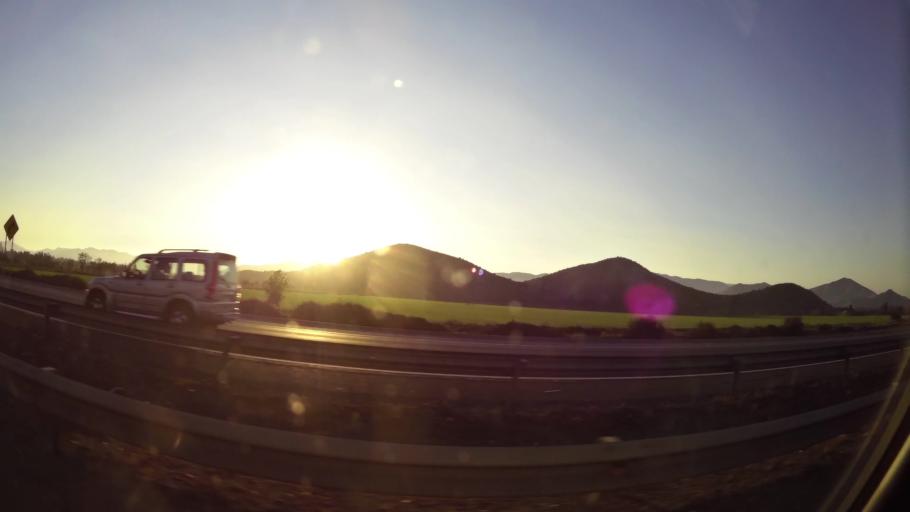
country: CL
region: Santiago Metropolitan
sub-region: Provincia de Talagante
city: Penaflor
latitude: -33.5415
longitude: -70.8036
